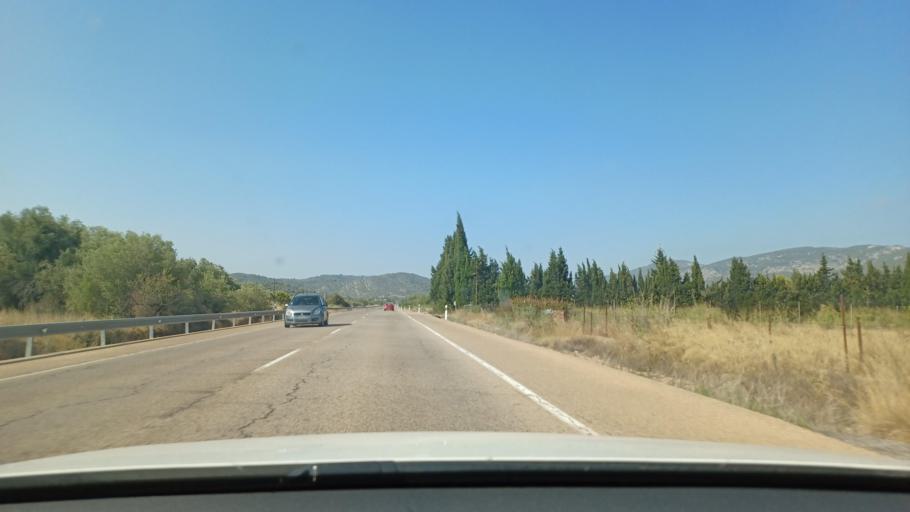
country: ES
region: Valencia
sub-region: Provincia de Castello
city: Alcala de Xivert
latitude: 40.2527
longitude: 0.2350
